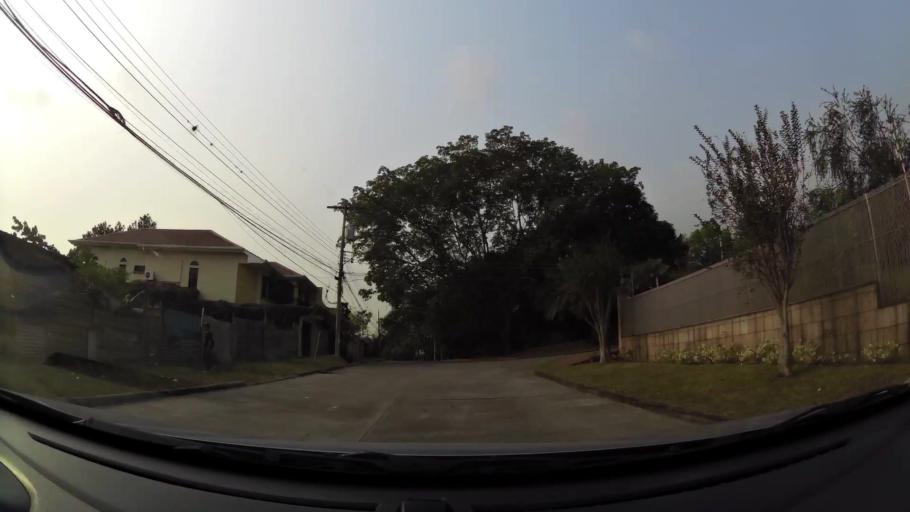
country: HN
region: Cortes
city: Armenta
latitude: 15.4918
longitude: -88.0466
